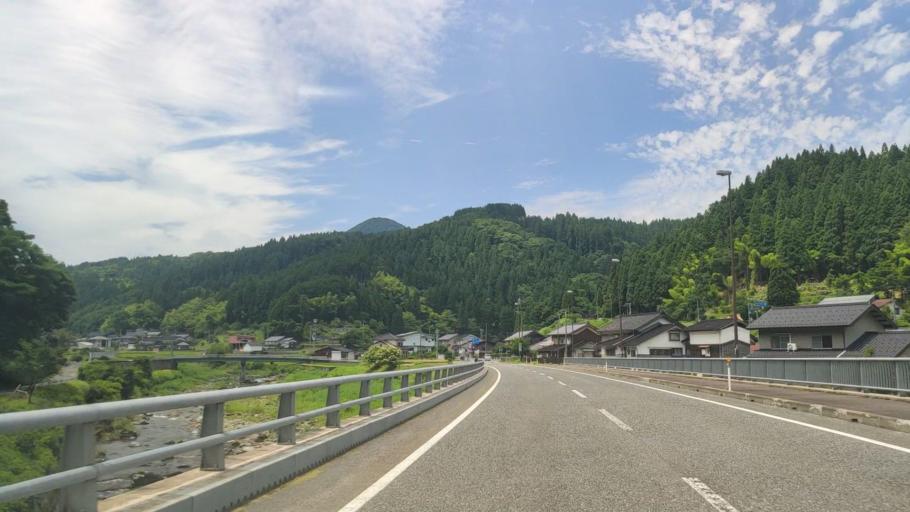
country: JP
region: Hyogo
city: Toyooka
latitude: 35.4892
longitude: 134.5568
